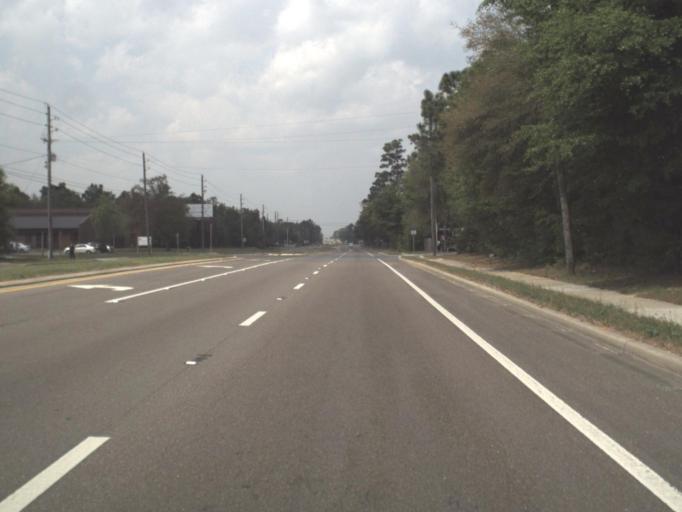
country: US
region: Florida
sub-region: Santa Rosa County
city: Point Baker
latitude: 30.6600
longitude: -87.0548
